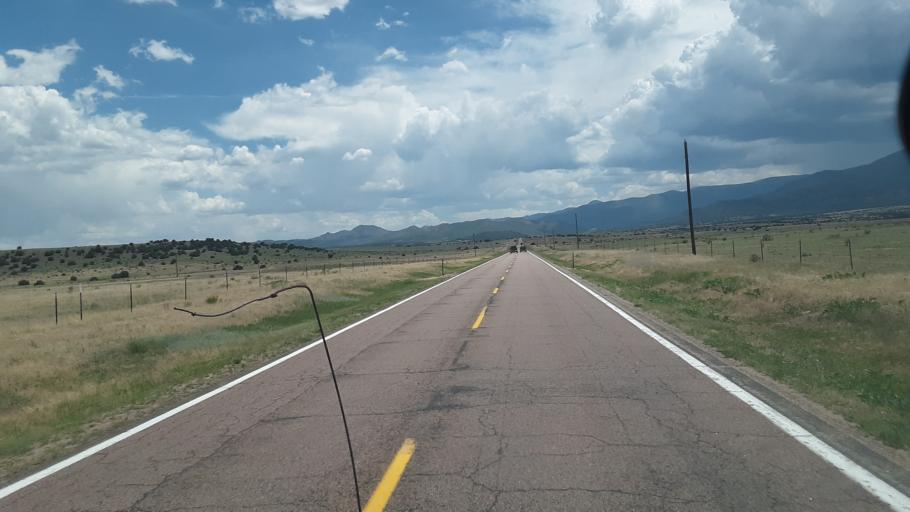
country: US
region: Colorado
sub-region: Fremont County
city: Florence
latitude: 38.2860
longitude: -105.0874
